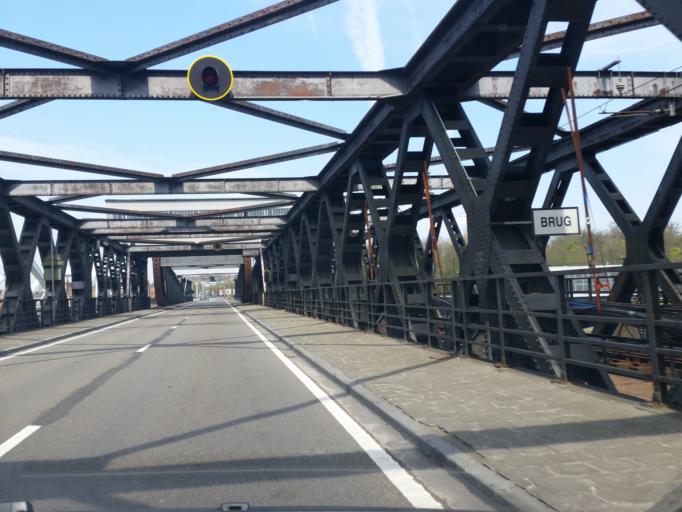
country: BE
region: Flanders
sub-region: Provincie Oost-Vlaanderen
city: Temse
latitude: 51.1210
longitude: 4.2194
